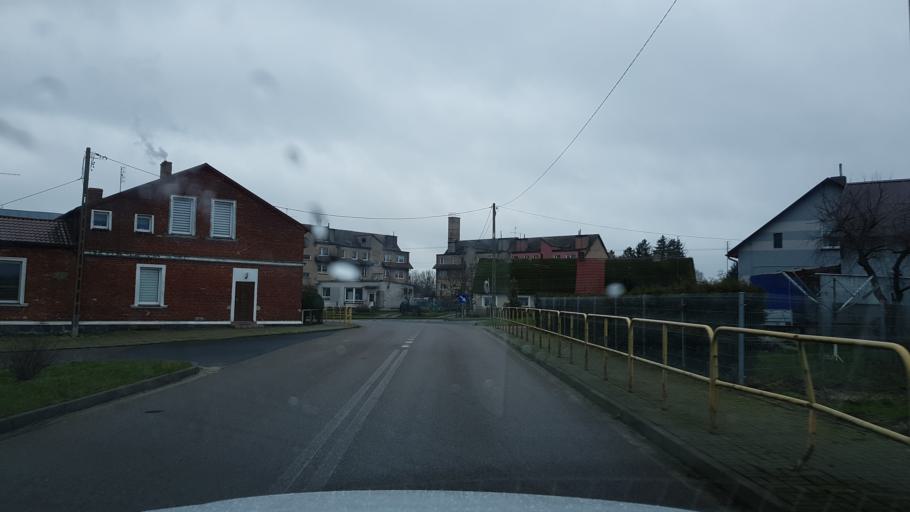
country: PL
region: West Pomeranian Voivodeship
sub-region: Powiat lobeski
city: Radowo Male
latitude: 53.6159
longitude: 15.4818
